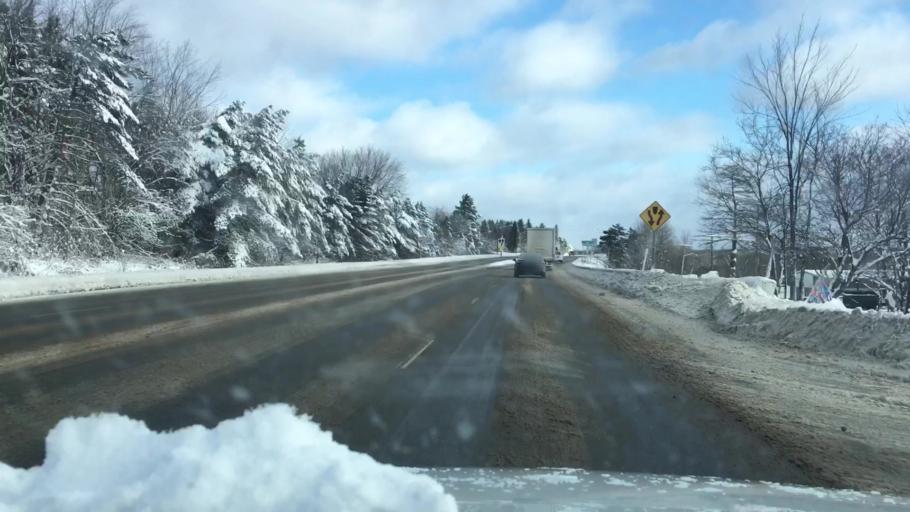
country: US
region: Maine
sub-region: Aroostook County
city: Caribou
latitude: 46.8586
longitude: -68.0047
